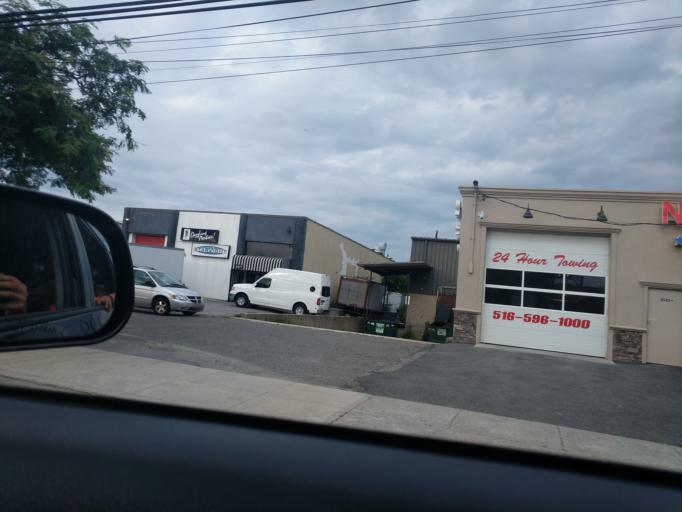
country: US
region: New York
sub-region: Nassau County
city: Oceanside
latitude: 40.6252
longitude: -73.6514
